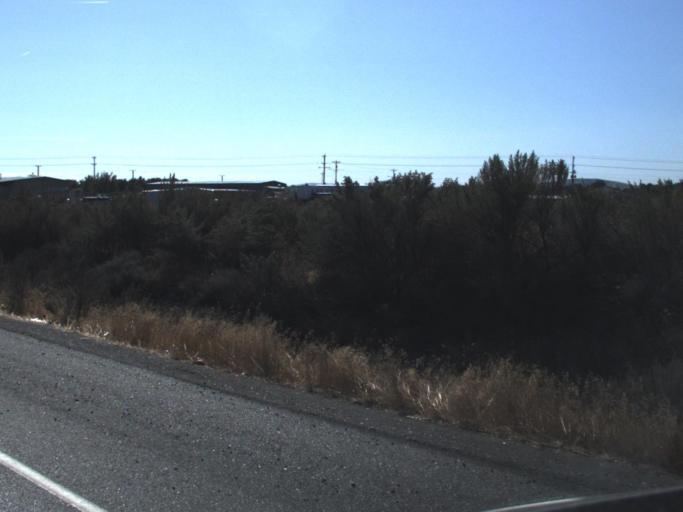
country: US
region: Washington
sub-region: Benton County
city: Richland
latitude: 46.3135
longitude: -119.2924
